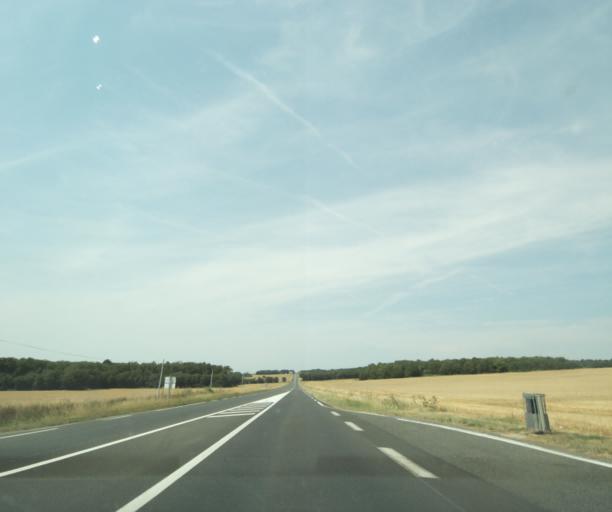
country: FR
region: Centre
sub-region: Departement d'Indre-et-Loire
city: Sainte-Maure-de-Touraine
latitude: 47.0770
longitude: 0.6131
